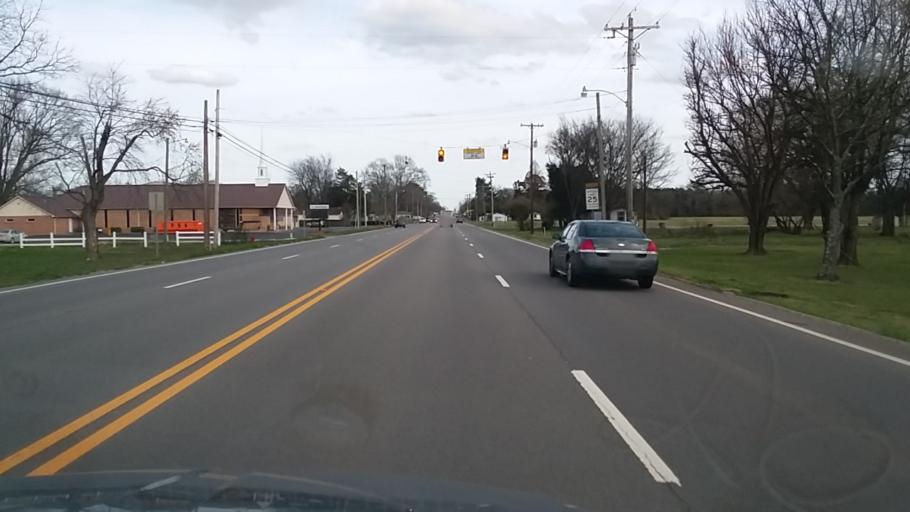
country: US
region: Alabama
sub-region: Lawrence County
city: Town Creek
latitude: 34.6814
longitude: -87.4162
